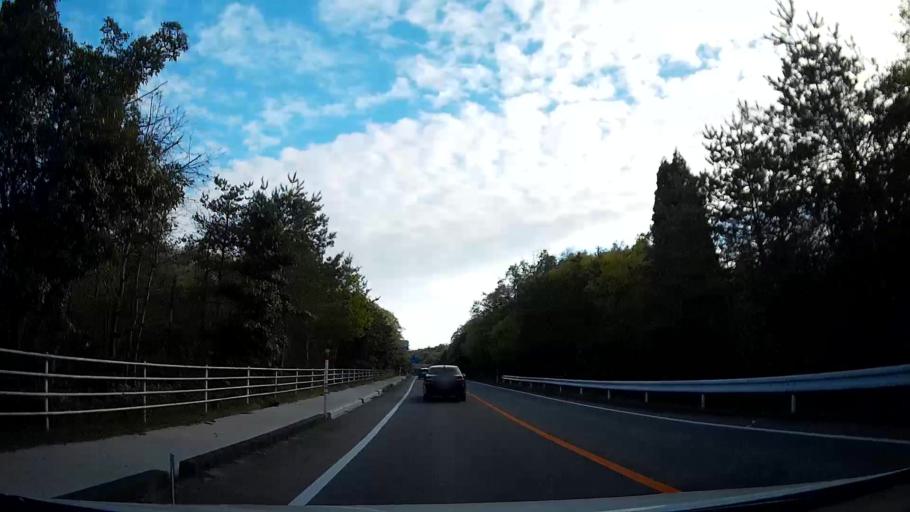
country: JP
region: Ishikawa
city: Nanao
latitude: 37.0660
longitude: 136.9190
